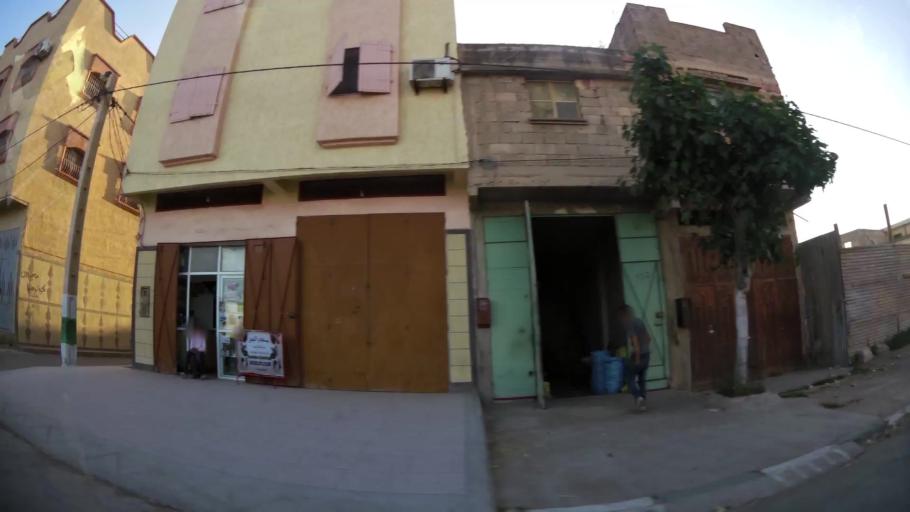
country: MA
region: Oriental
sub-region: Oujda-Angad
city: Oujda
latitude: 34.7109
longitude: -1.9090
